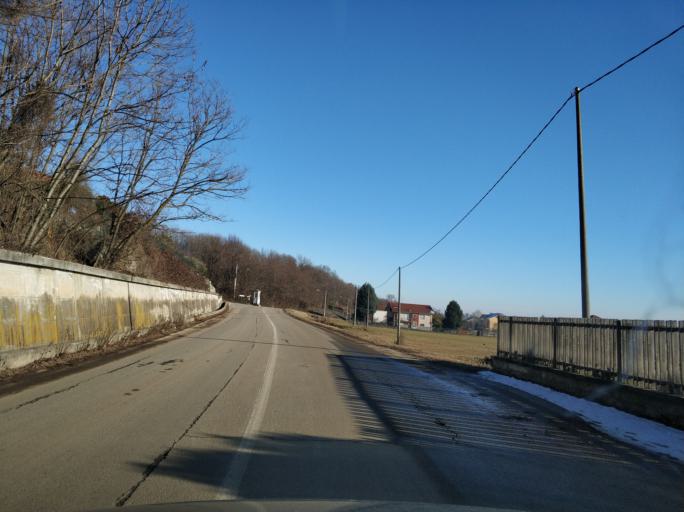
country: IT
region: Piedmont
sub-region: Provincia di Torino
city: San Francesco al Campo
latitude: 45.2231
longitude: 7.6595
